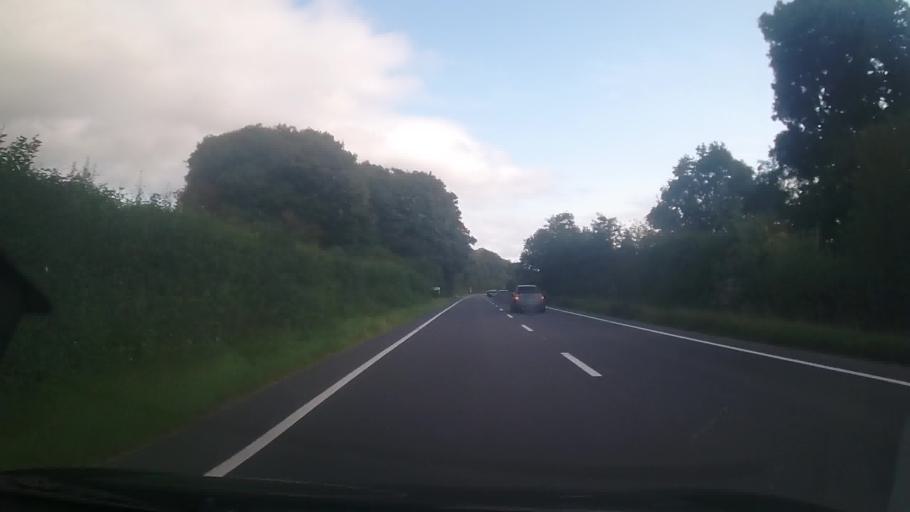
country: GB
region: England
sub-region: Shropshire
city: Craven Arms
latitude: 52.4145
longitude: -2.8123
